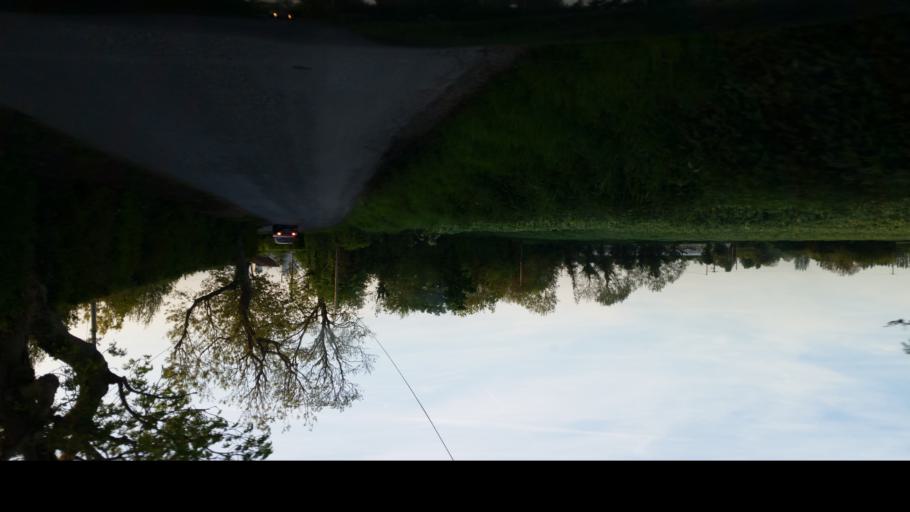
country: IE
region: Leinster
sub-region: Fingal County
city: Swords
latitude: 53.4864
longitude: -6.2199
